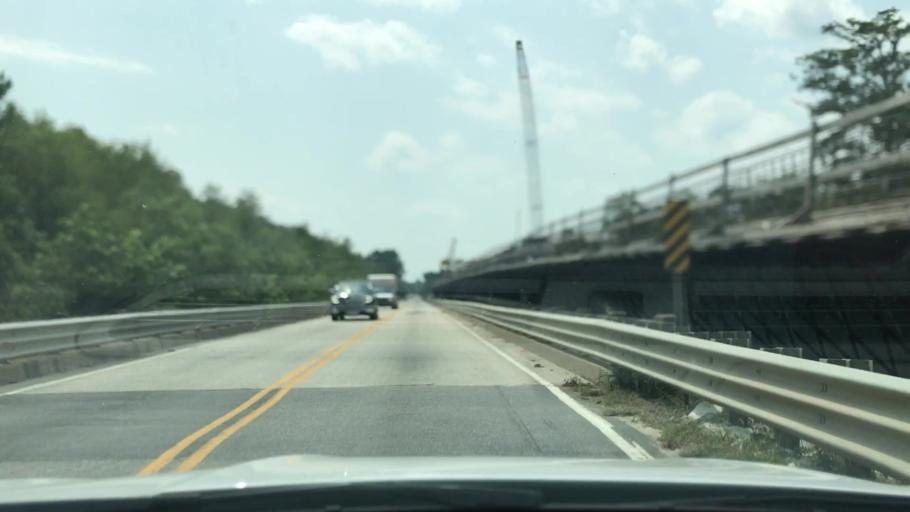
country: US
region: South Carolina
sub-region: Georgetown County
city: Murrells Inlet
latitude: 33.6568
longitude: -79.1597
